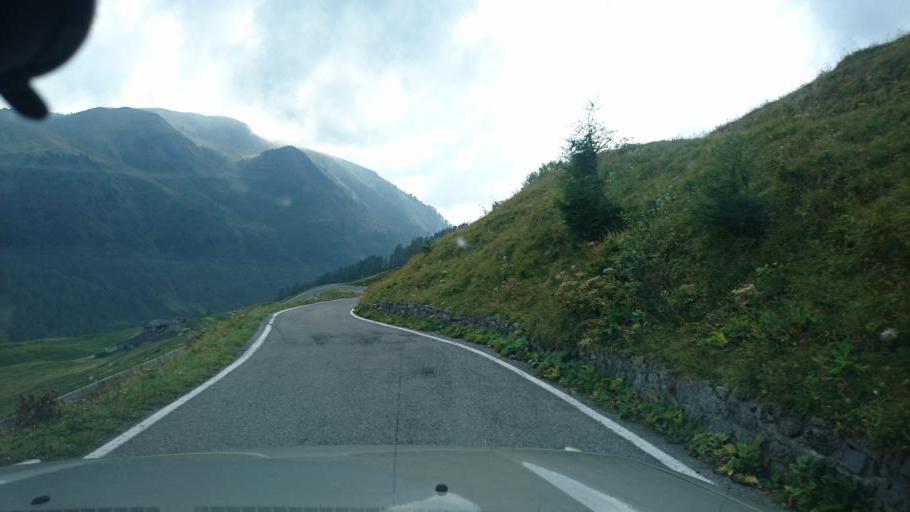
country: IT
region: Lombardy
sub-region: Provincia di Brescia
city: Bagolino
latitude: 45.9148
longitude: 10.4247
